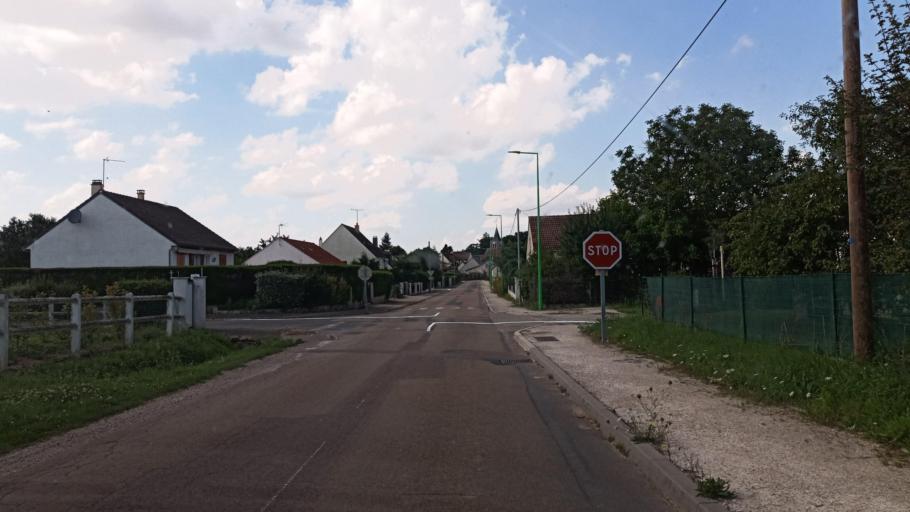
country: FR
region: Bourgogne
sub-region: Departement de l'Yonne
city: Saint-Valerien
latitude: 48.1756
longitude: 3.0973
